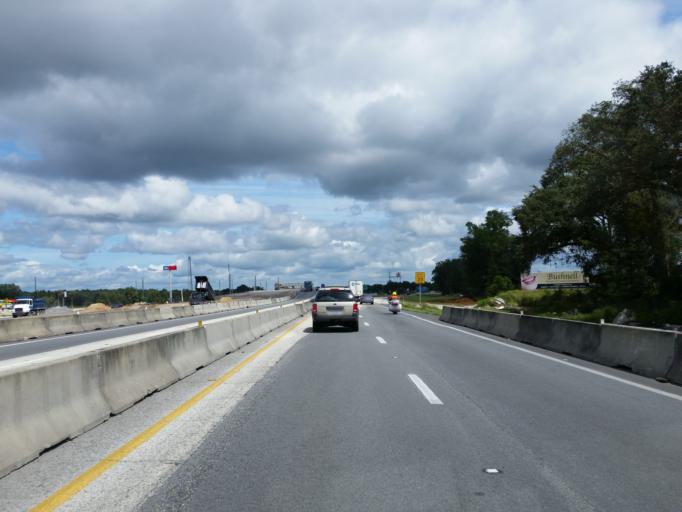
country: US
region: Florida
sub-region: Sumter County
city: Bushnell
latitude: 28.6647
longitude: -82.1453
